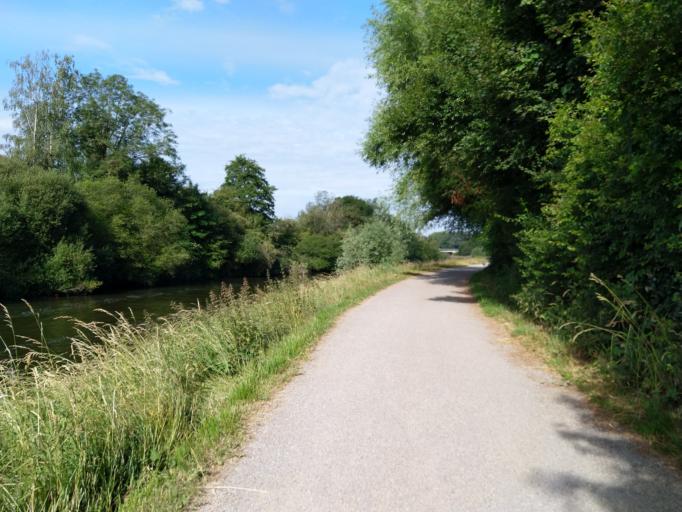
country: FR
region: Nord-Pas-de-Calais
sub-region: Departement du Nord
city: Rousies
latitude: 50.2753
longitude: 3.9897
